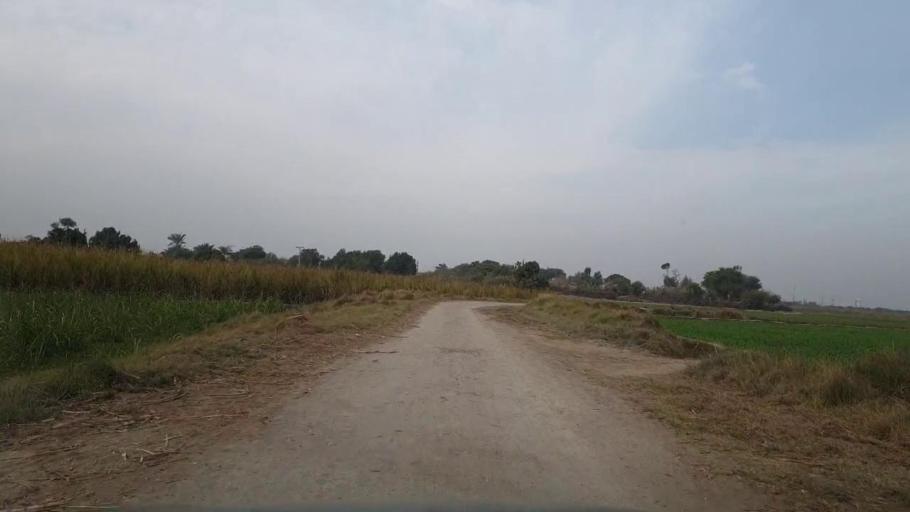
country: PK
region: Sindh
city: Matiari
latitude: 25.5626
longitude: 68.5405
